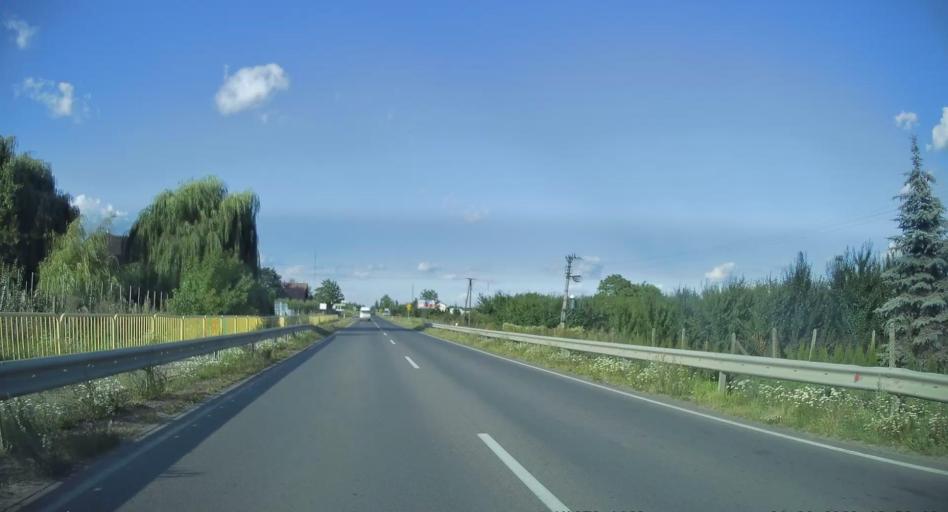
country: PL
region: Masovian Voivodeship
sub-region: Powiat grojecki
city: Grojec
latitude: 51.8498
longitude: 20.8403
